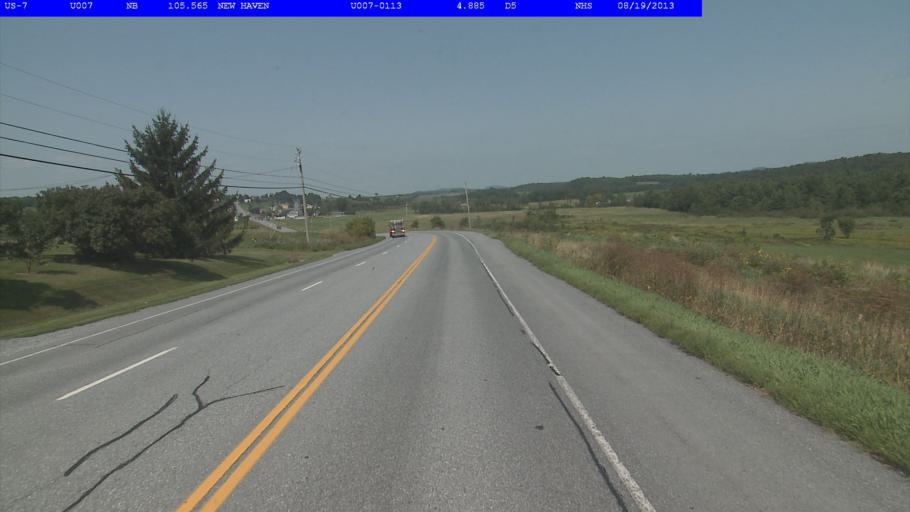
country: US
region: Vermont
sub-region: Addison County
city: Vergennes
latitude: 44.1156
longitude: -73.1762
